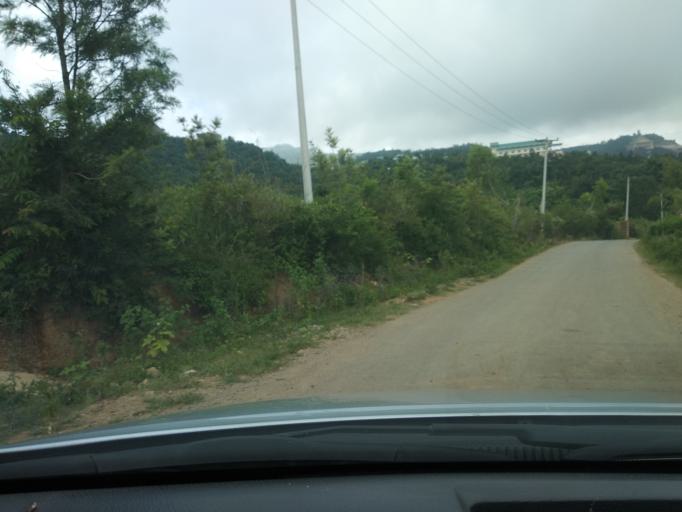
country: MM
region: Mandalay
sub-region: Pyin Oo Lwin District
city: Pyin Oo Lwin
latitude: 21.9183
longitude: 96.3831
